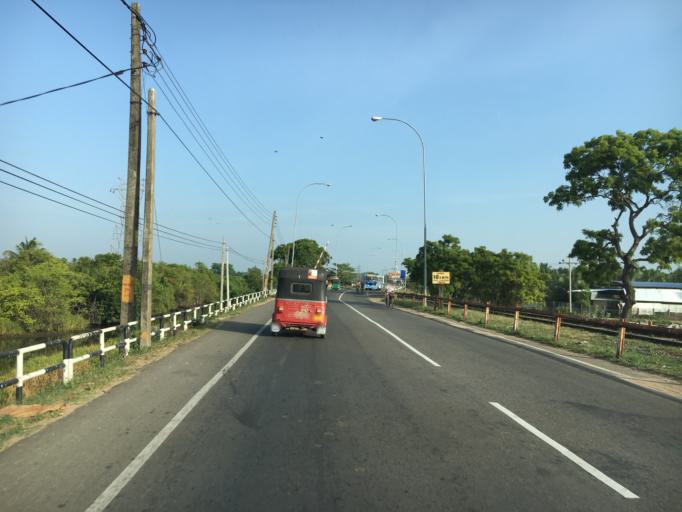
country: LK
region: Eastern Province
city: Eravur Town
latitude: 7.9191
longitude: 81.5175
